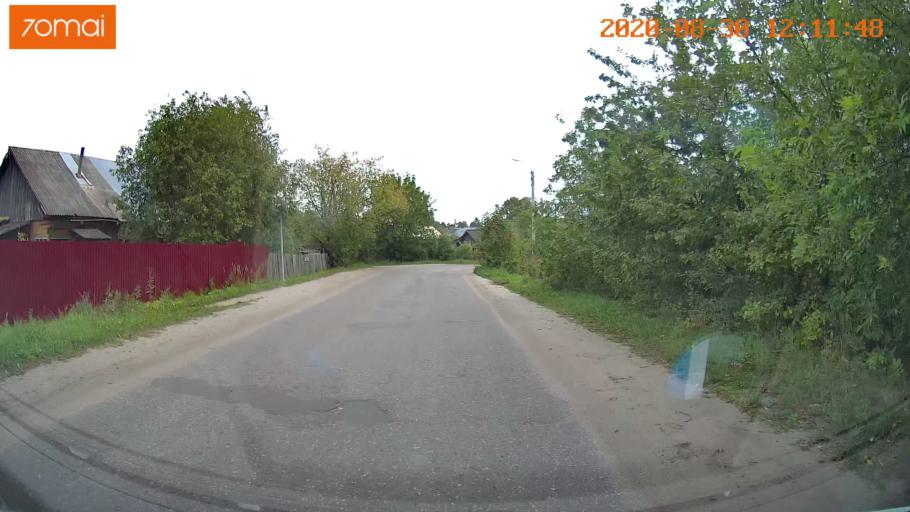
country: RU
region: Ivanovo
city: Yur'yevets
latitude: 57.3118
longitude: 43.0964
